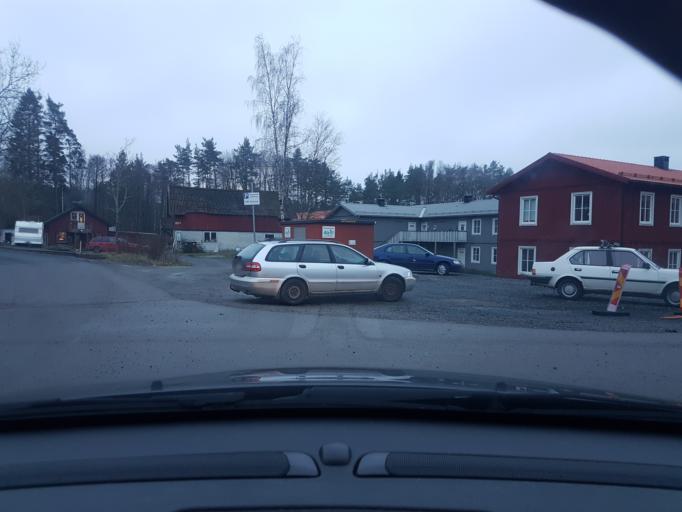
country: SE
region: Vaestra Goetaland
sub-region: Ale Kommun
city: Alvangen
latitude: 57.9484
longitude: 12.1212
